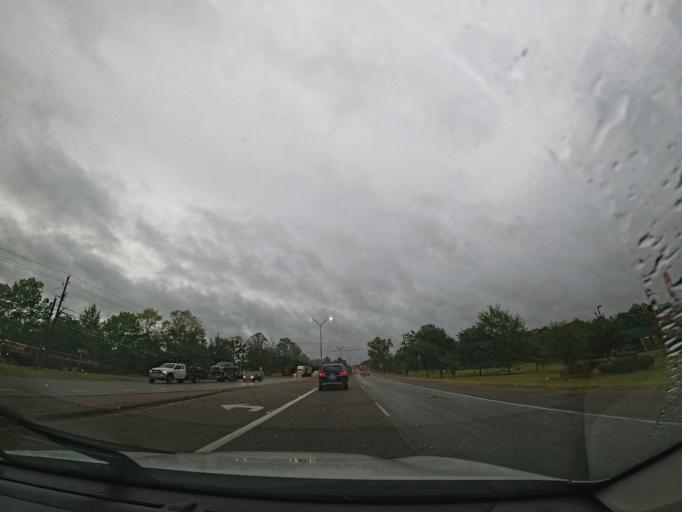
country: US
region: Texas
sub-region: Angelina County
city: Diboll
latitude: 31.1927
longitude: -94.7805
